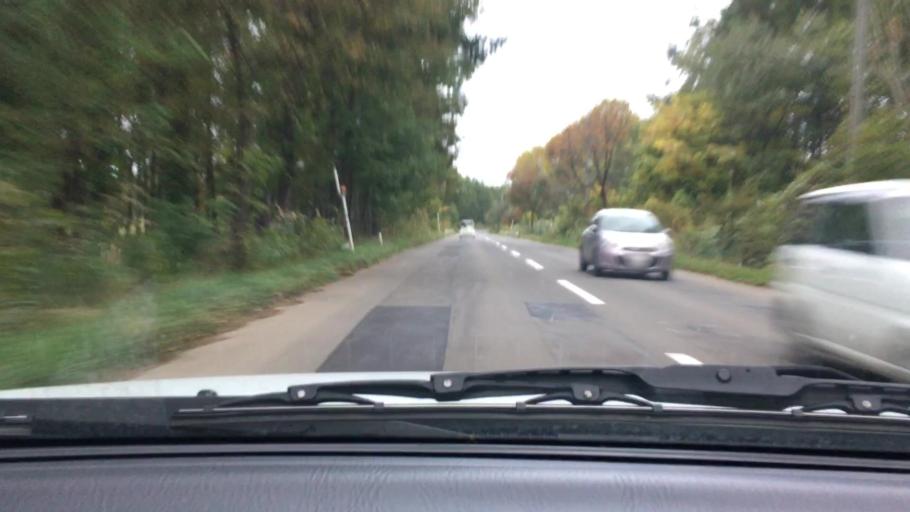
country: JP
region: Aomori
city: Shimokizukuri
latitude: 40.7161
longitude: 140.2991
